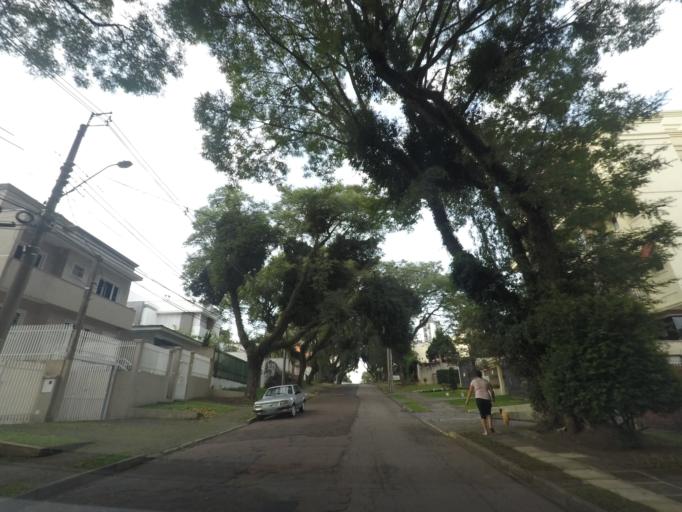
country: BR
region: Parana
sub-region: Curitiba
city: Curitiba
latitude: -25.4271
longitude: -49.2961
